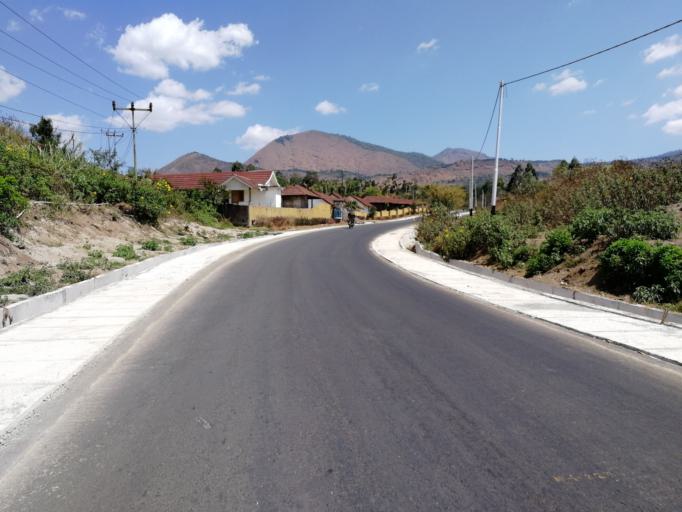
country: ID
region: West Nusa Tenggara
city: Sembalunlawang
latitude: -8.3552
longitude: 116.5138
